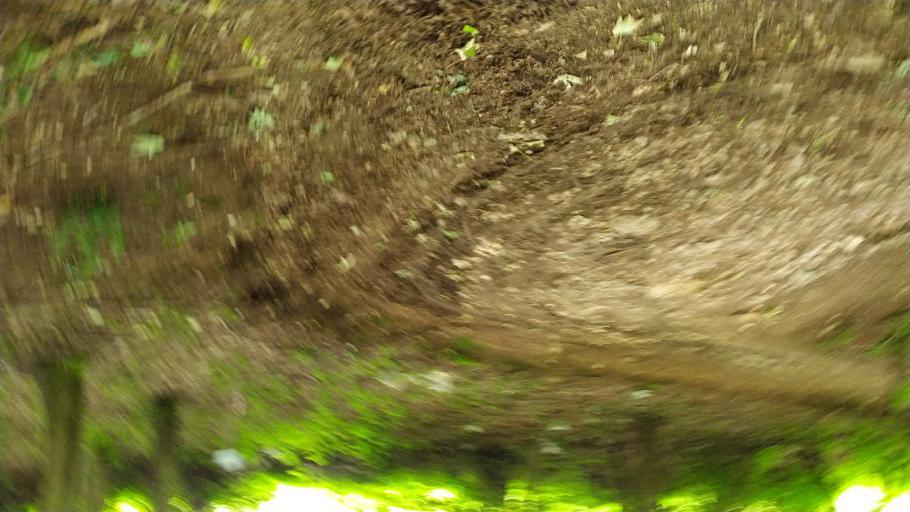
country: IT
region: Veneto
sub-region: Provincia di Vicenza
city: Torrebelvicino
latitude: 45.6934
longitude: 11.3107
